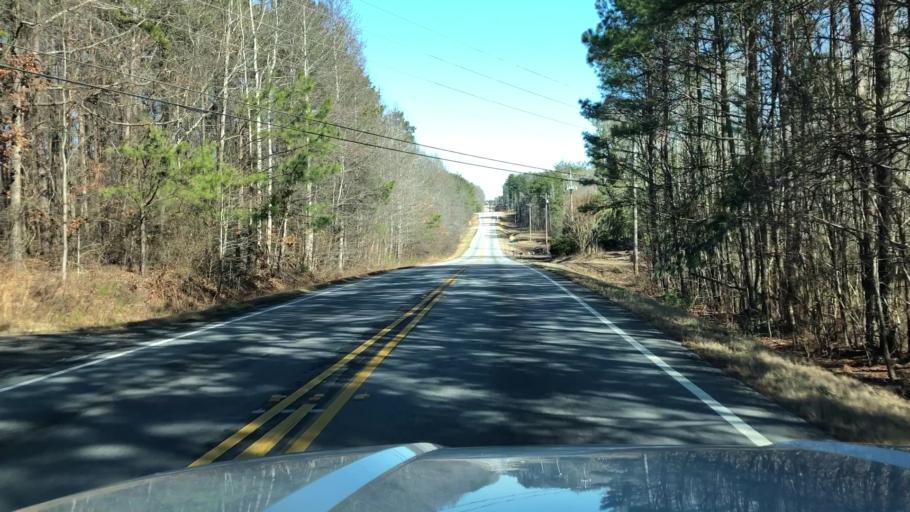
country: US
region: Georgia
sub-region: Cobb County
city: Acworth
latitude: 34.0158
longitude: -84.7515
